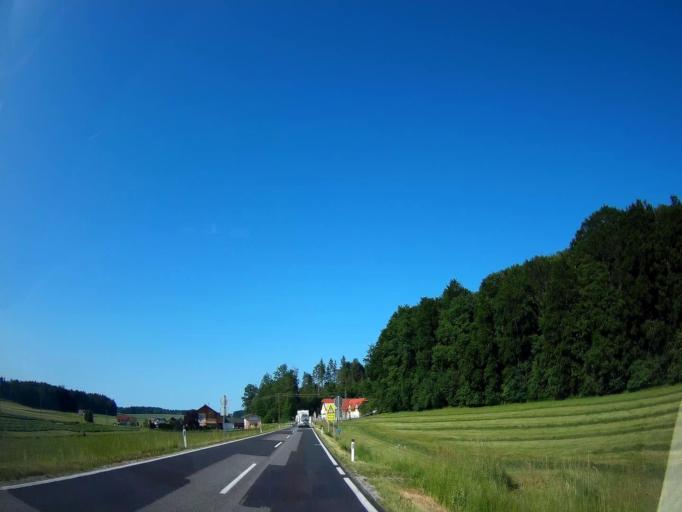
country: AT
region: Salzburg
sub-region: Politischer Bezirk Salzburg-Umgebung
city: Dorfbeuern
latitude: 48.1053
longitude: 12.9978
